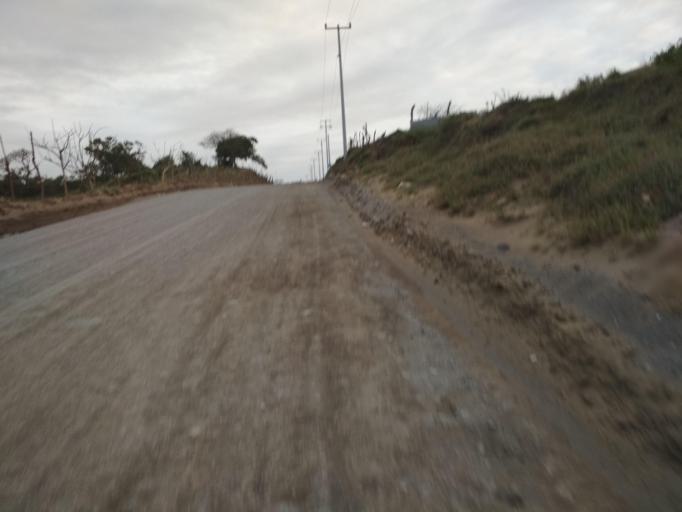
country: MX
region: Veracruz
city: Anton Lizardo
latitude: 19.0468
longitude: -95.9928
